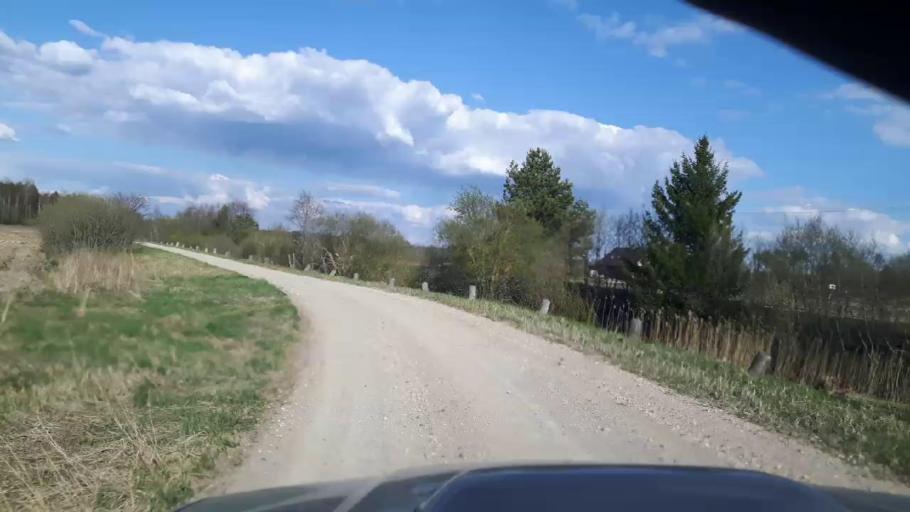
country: EE
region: Paernumaa
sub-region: Tootsi vald
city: Tootsi
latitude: 58.4141
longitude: 24.8445
